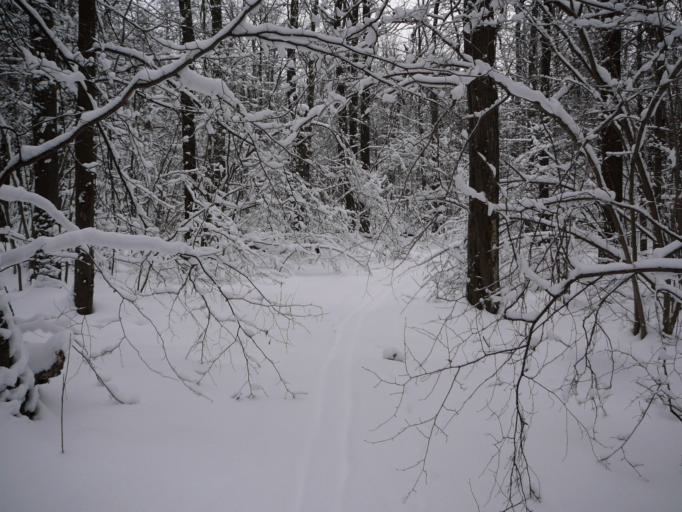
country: RU
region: Moskovskaya
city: Odintsovo
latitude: 55.6895
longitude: 37.2476
